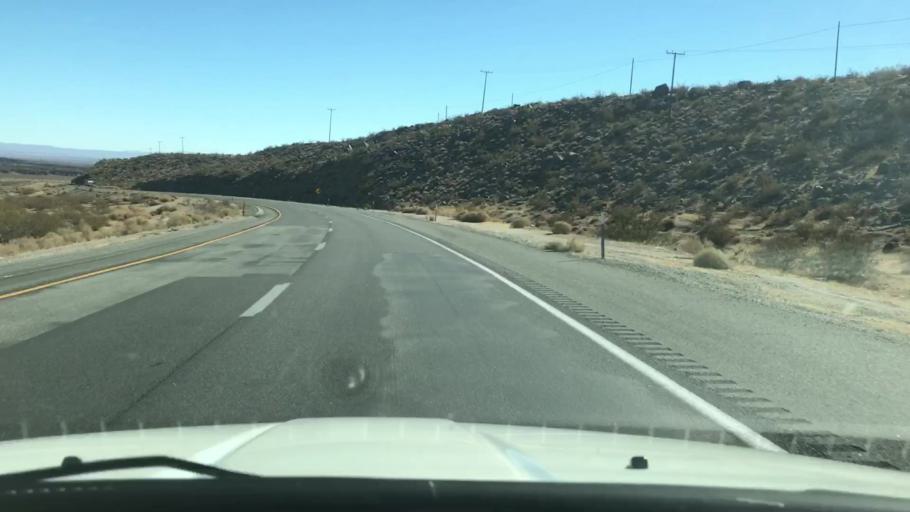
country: US
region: California
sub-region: Kern County
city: Inyokern
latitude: 35.8721
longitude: -117.8877
